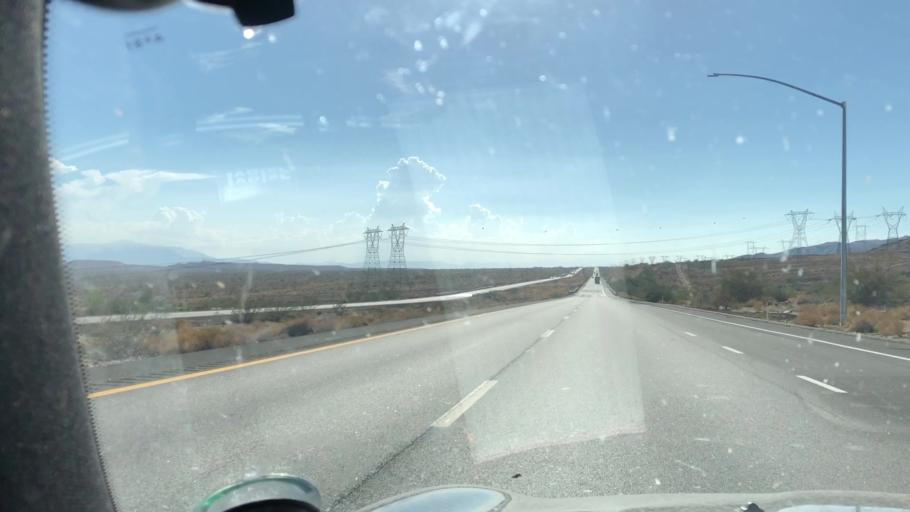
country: US
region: California
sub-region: Riverside County
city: Mecca
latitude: 33.6701
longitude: -115.9145
